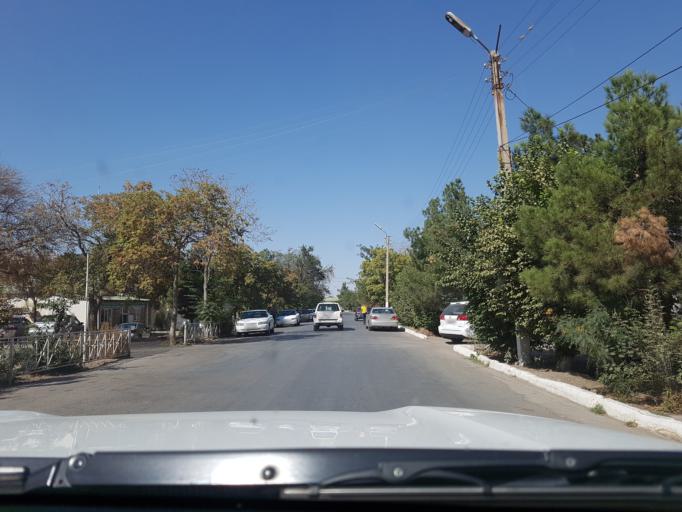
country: IR
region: Razavi Khorasan
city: Sarakhs
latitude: 36.5256
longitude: 61.2138
